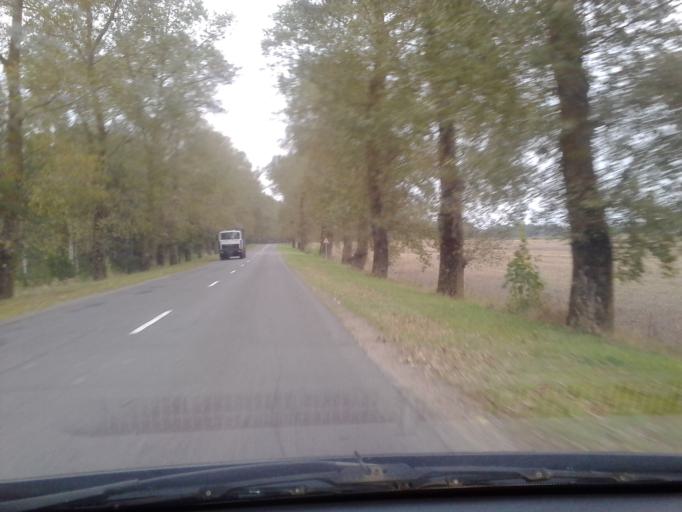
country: BY
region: Vitebsk
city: Pastavy
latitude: 55.1551
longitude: 26.9759
